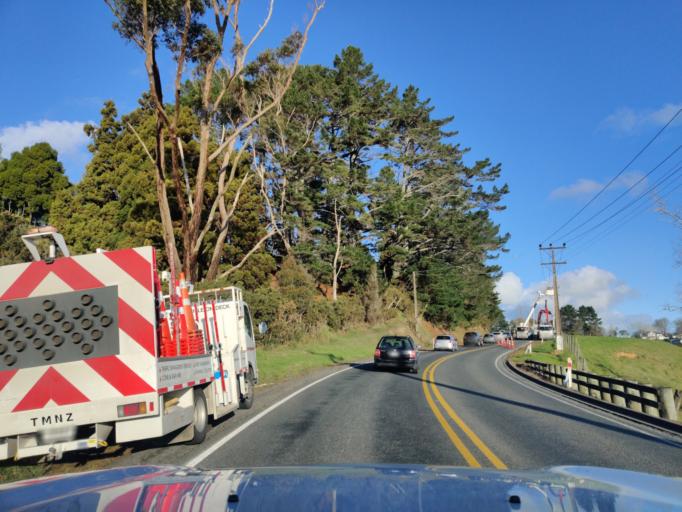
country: NZ
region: Auckland
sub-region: Auckland
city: Red Hill
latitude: -36.9688
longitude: 174.9850
